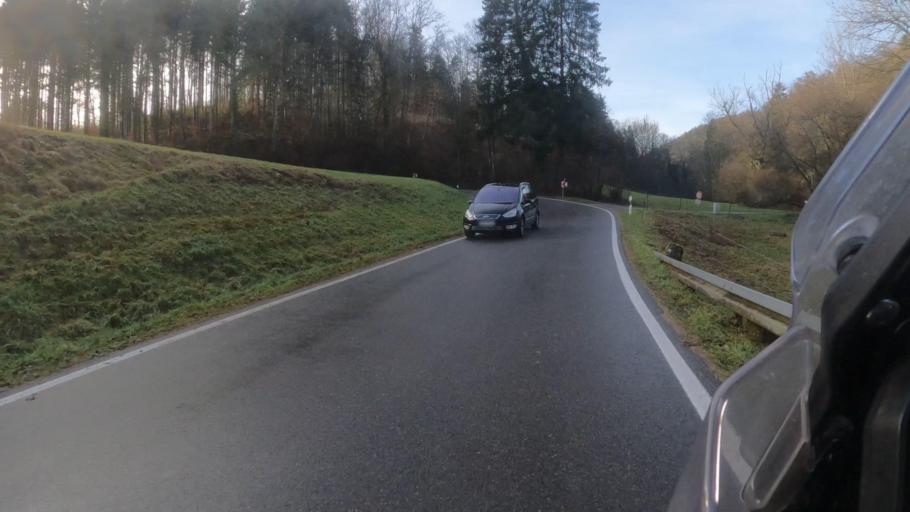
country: DE
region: Baden-Wuerttemberg
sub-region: Freiburg Region
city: Tengen
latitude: 47.8072
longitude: 8.6600
